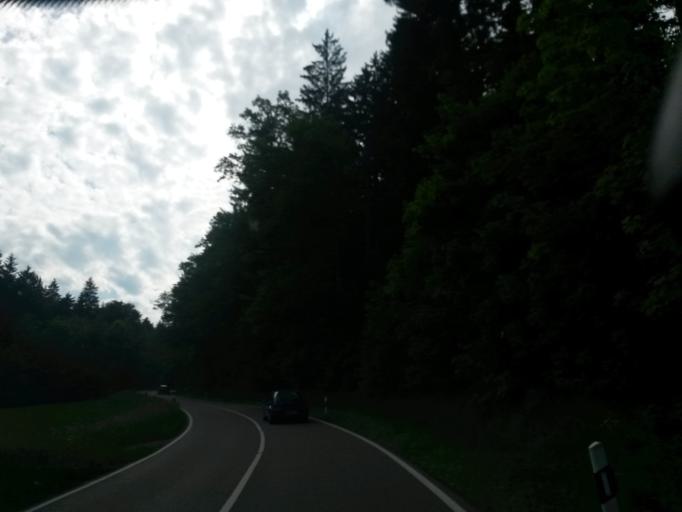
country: DE
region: Baden-Wuerttemberg
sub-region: Karlsruhe Region
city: Oberreichenbach
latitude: 48.7348
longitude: 8.6790
